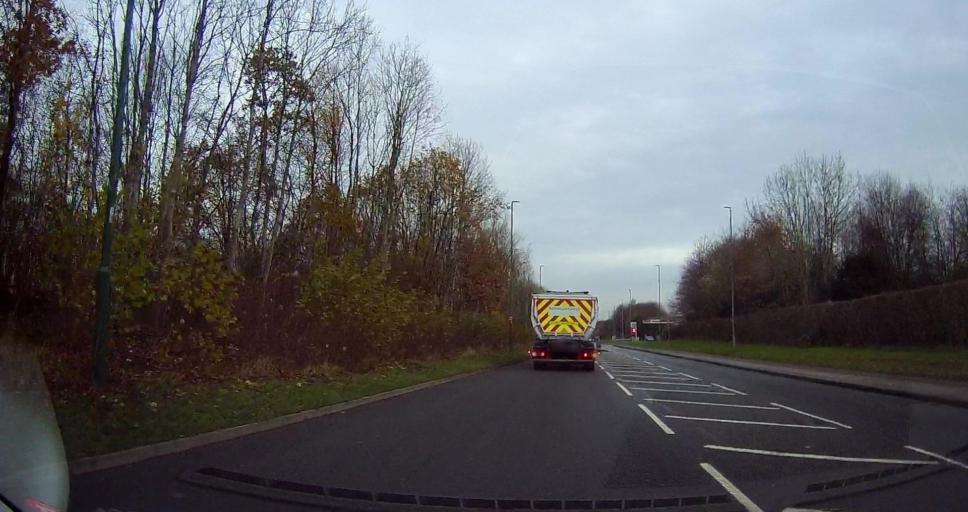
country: GB
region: England
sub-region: Nottinghamshire
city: Kimberley
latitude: 52.9837
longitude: -1.2335
